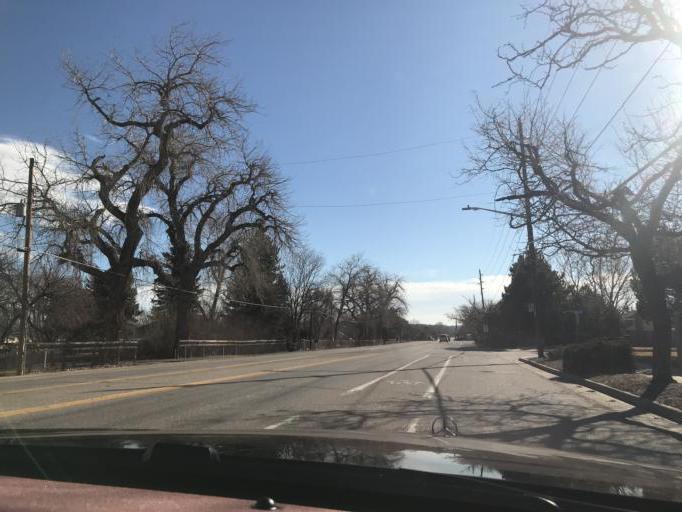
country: US
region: Colorado
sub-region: Jefferson County
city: Applewood
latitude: 39.8270
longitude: -105.1591
